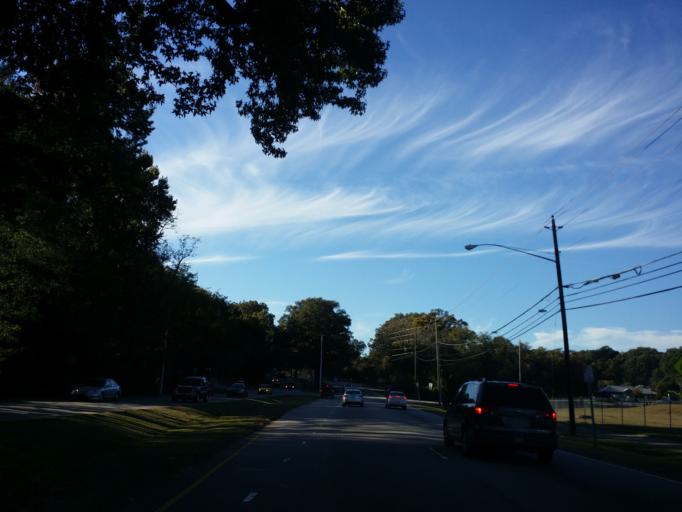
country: US
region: North Carolina
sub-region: Wake County
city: West Raleigh
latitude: 35.7772
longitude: -78.6617
